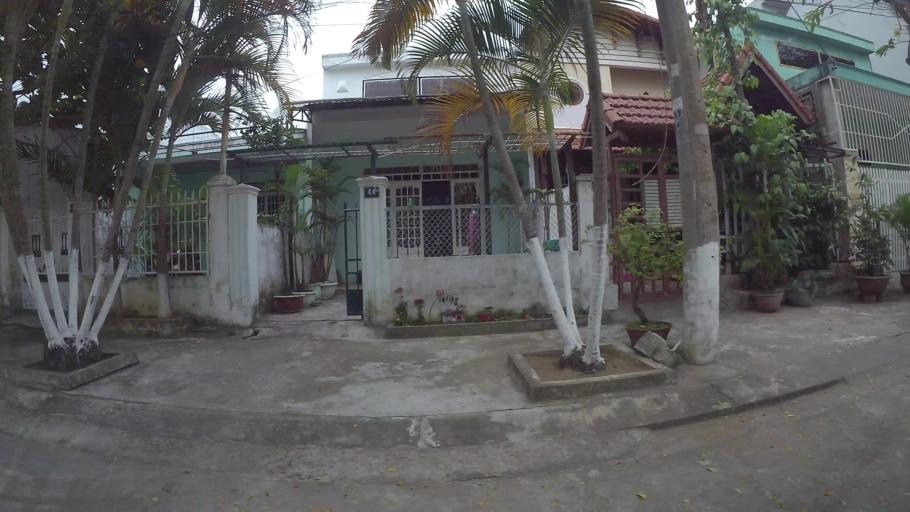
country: VN
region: Da Nang
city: Cam Le
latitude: 16.0280
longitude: 108.2120
